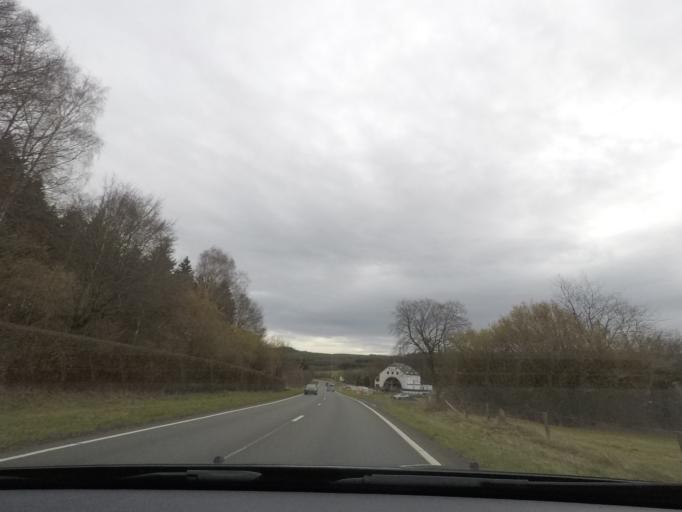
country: BE
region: Wallonia
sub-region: Province du Luxembourg
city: Bastogne
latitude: 49.9810
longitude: 5.7628
